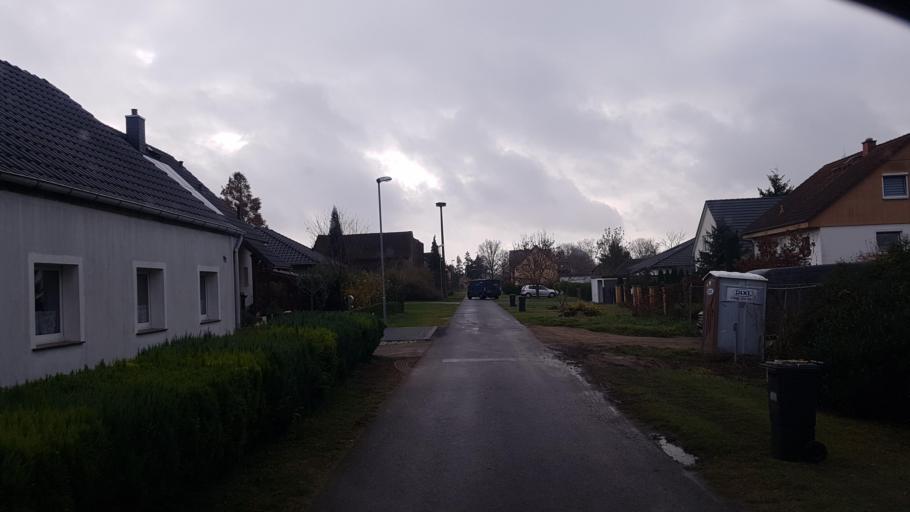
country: DE
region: Brandenburg
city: Roskow
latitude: 52.4117
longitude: 12.6901
